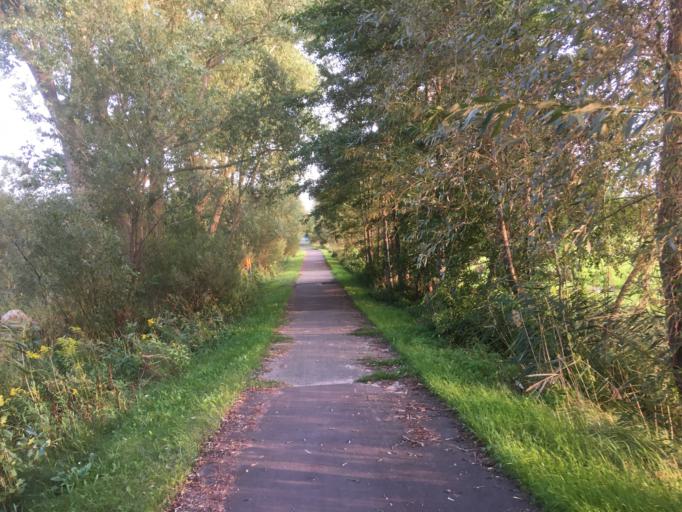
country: DE
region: Brandenburg
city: Erkner
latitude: 52.3839
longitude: 13.7800
